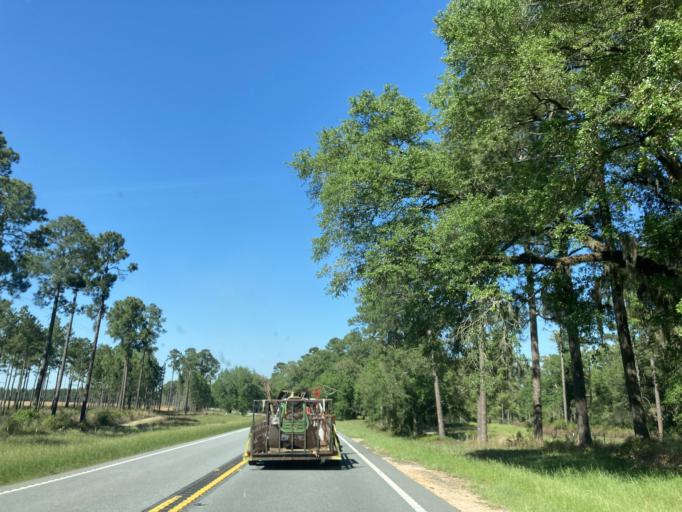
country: US
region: Georgia
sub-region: Baker County
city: Newton
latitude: 31.3708
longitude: -84.2864
